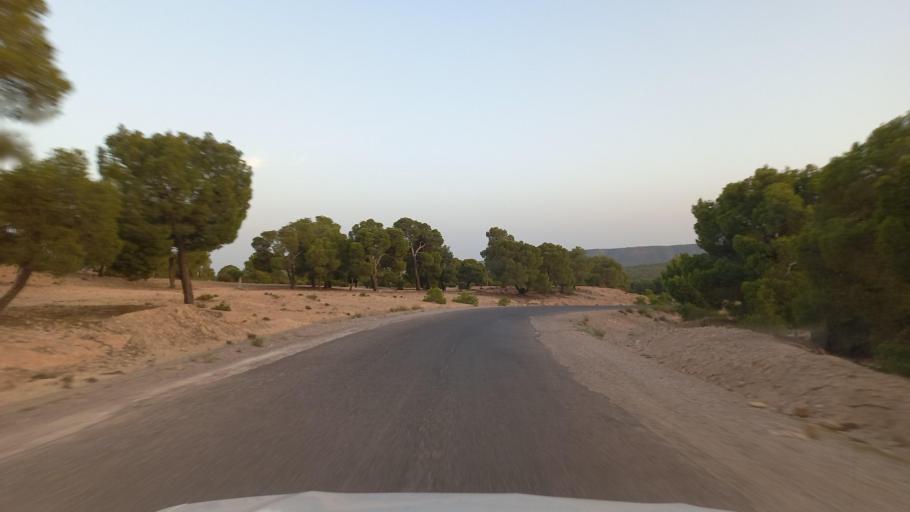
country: TN
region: Al Qasrayn
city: Sbiba
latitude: 35.4217
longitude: 8.9239
